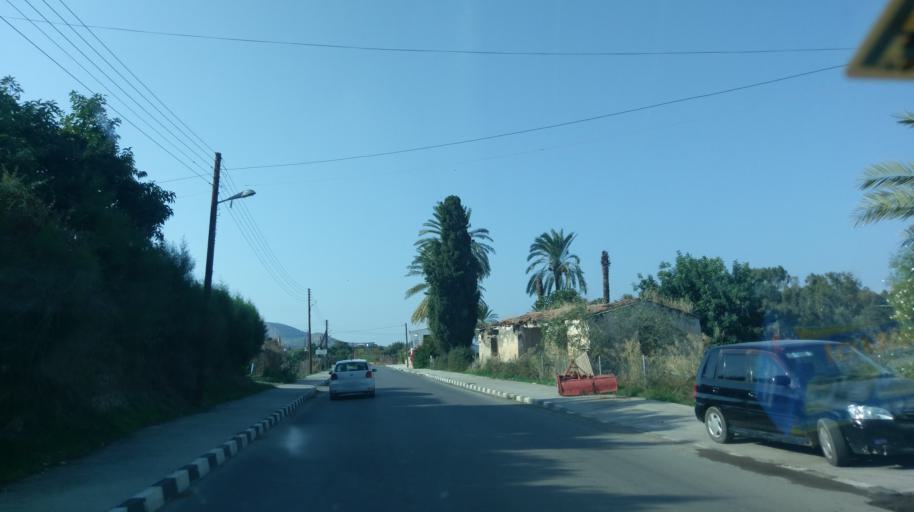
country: CY
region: Lefkosia
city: Lefka
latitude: 35.1417
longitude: 32.8148
